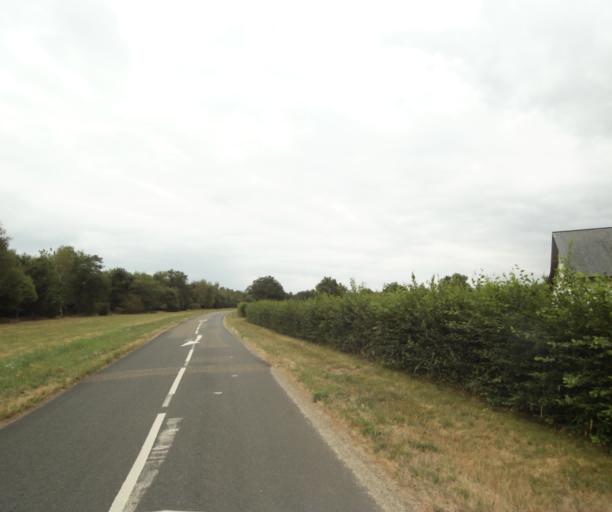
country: FR
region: Pays de la Loire
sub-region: Departement de la Sarthe
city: Sable-sur-Sarthe
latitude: 47.8179
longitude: -0.3531
